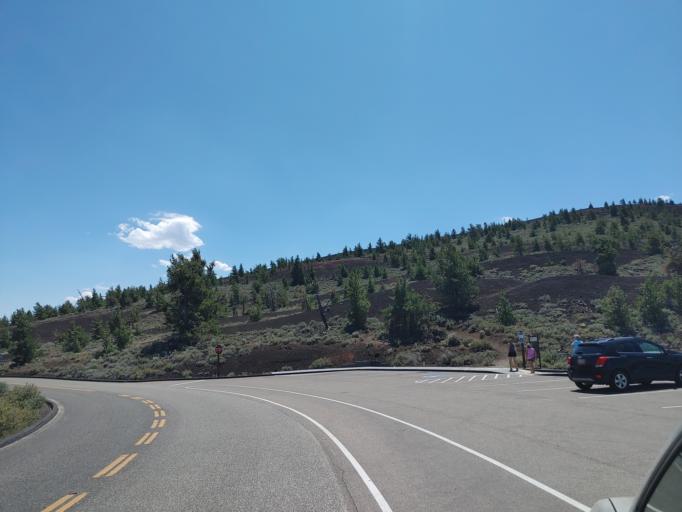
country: US
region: Idaho
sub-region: Butte County
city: Arco
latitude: 43.4563
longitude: -113.5592
